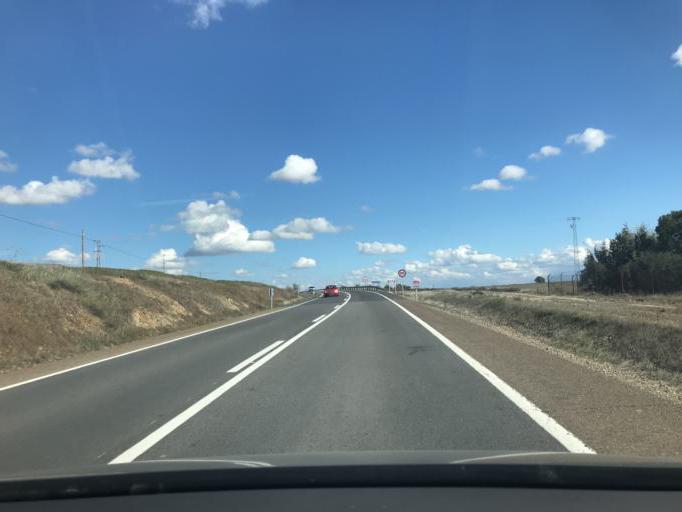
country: ES
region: Extremadura
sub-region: Provincia de Badajoz
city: Granja de Torrehermosa
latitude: 38.2979
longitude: -5.6311
